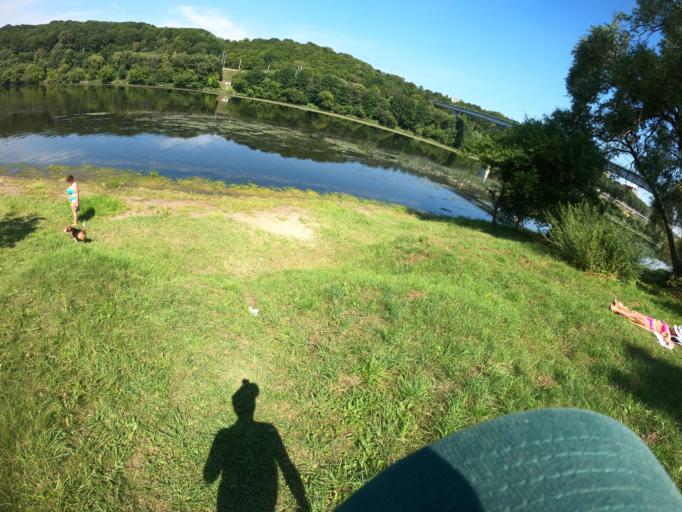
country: LT
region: Kauno apskritis
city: Dainava (Kaunas)
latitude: 54.8932
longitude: 23.9685
